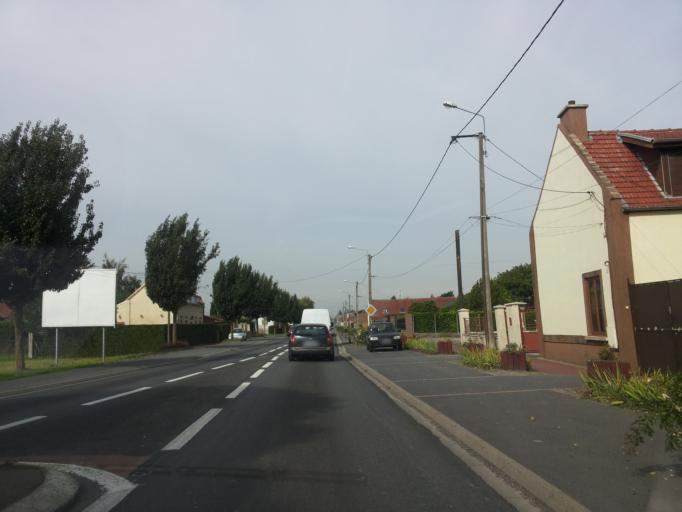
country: FR
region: Nord-Pas-de-Calais
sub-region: Departement du Nord
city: Raillencourt-Sainte-Olle
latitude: 50.1871
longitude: 3.1808
